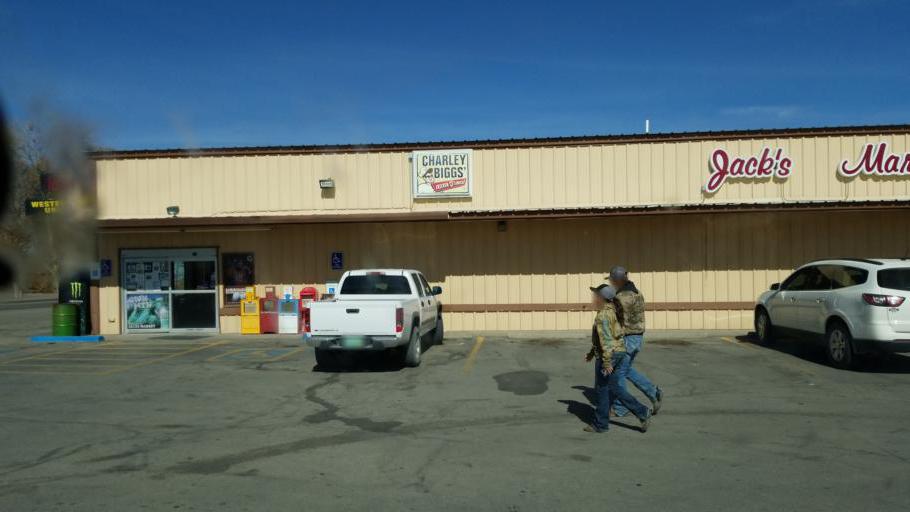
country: US
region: Colorado
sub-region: Conejos County
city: Conejos
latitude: 37.2774
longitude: -105.9610
